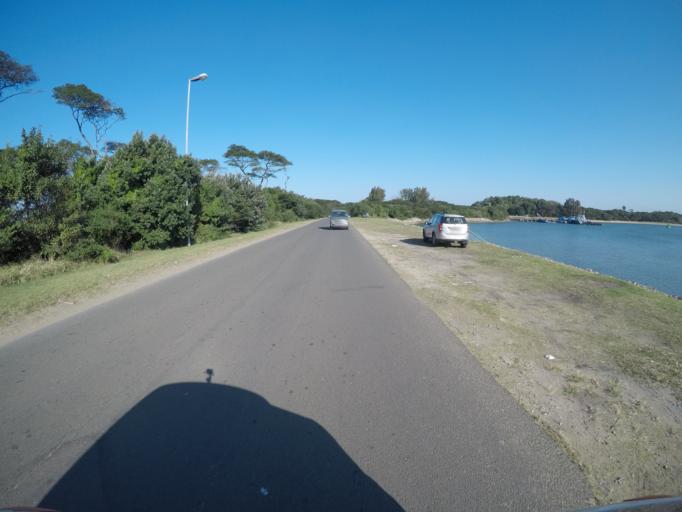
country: ZA
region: KwaZulu-Natal
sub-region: uThungulu District Municipality
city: Richards Bay
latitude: -28.7968
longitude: 32.0821
